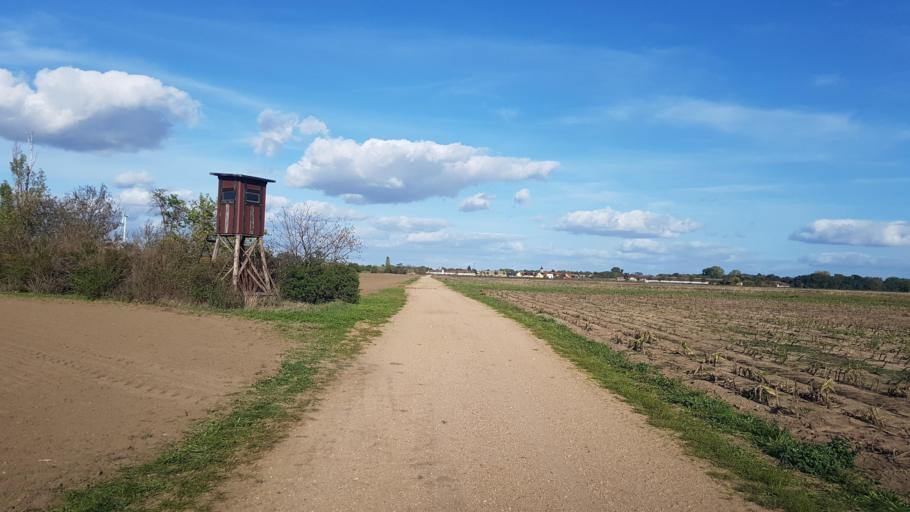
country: DE
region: Saxony
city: Nauwalde
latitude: 51.4486
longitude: 13.3243
